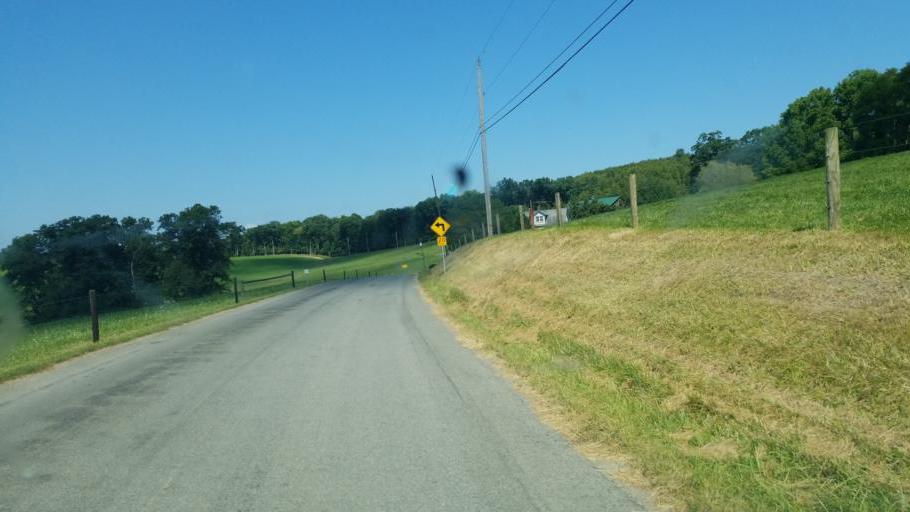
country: US
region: Pennsylvania
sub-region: Clarion County
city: Clarion
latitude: 41.1763
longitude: -79.4081
